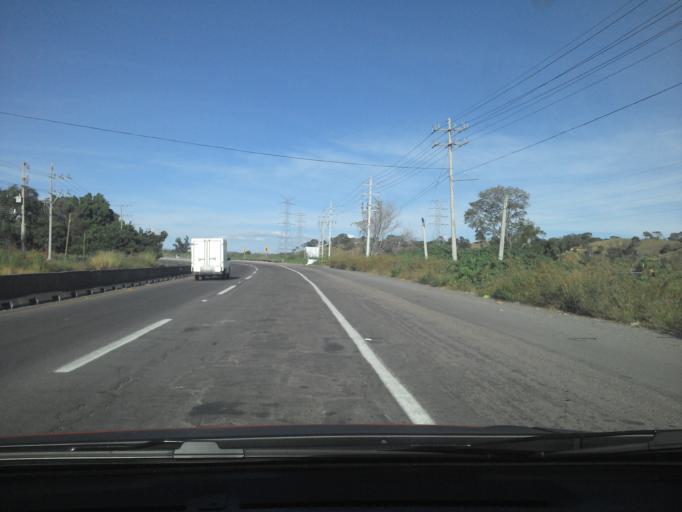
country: MX
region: Jalisco
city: Tala
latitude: 20.6810
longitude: -103.6969
